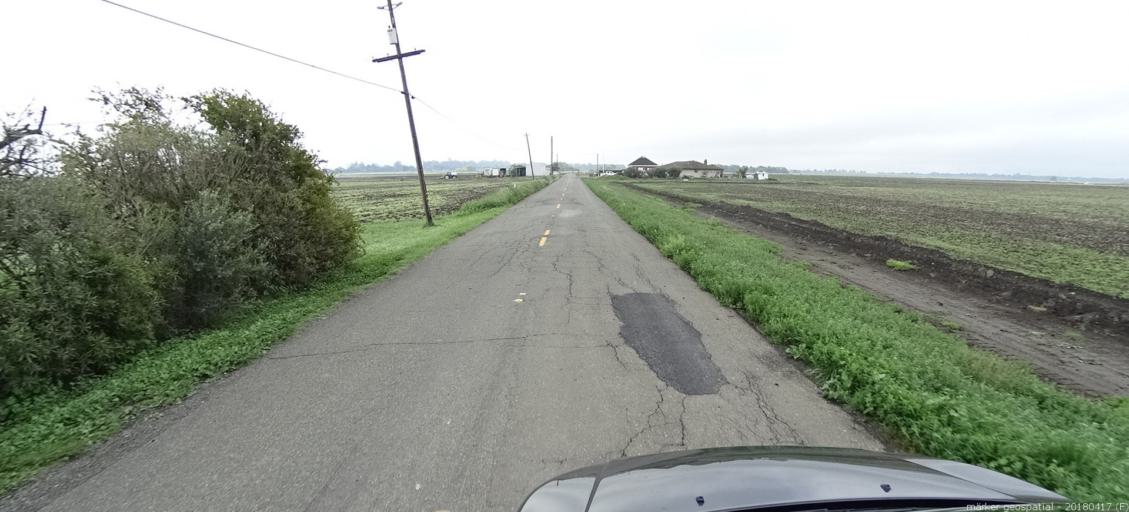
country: US
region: California
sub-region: Sacramento County
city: Walnut Grove
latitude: 38.1950
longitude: -121.5953
